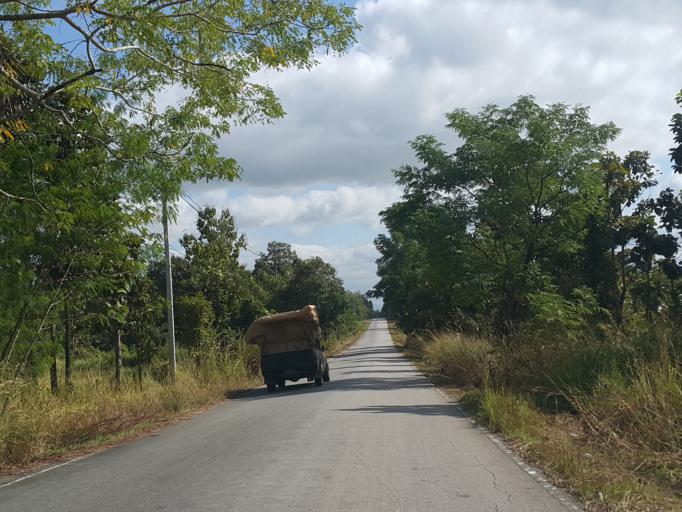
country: TH
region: Lampang
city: Hang Chat
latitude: 18.3373
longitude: 99.3819
